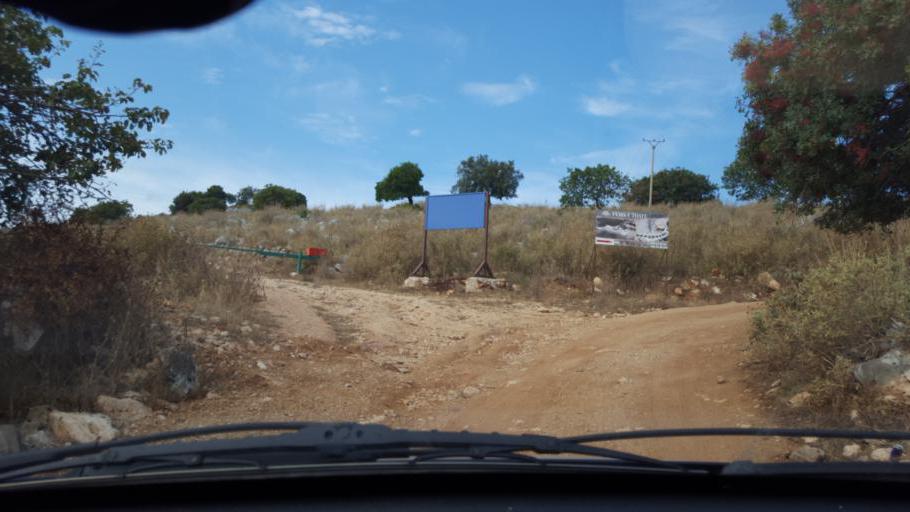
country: AL
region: Vlore
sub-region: Rrethi i Sarandes
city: Xarre
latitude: 39.7549
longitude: 19.9817
